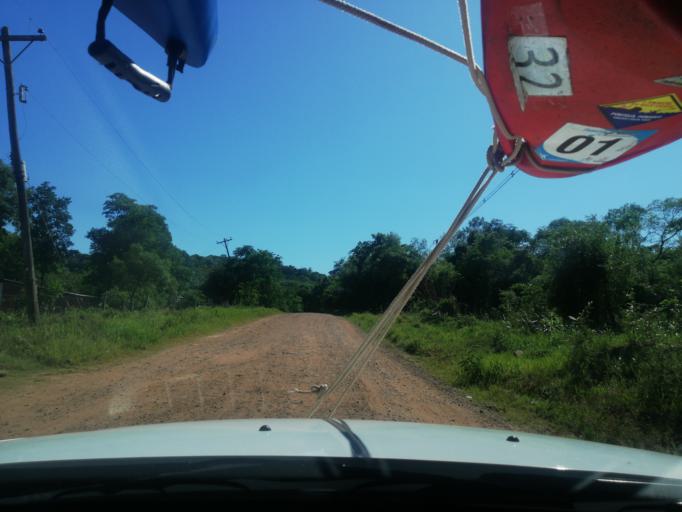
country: AR
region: Misiones
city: Santa Ana
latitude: -27.3364
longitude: -55.5830
